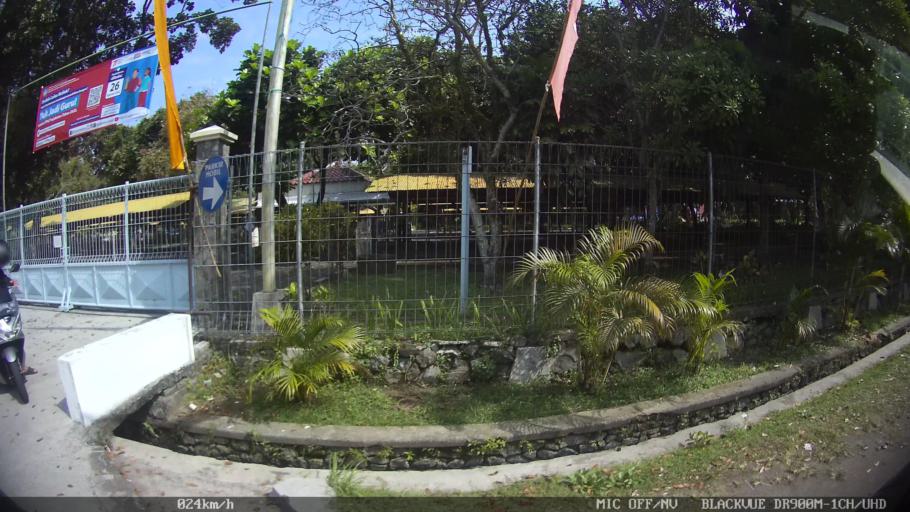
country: ID
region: Daerah Istimewa Yogyakarta
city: Depok
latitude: -7.7533
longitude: 110.4228
